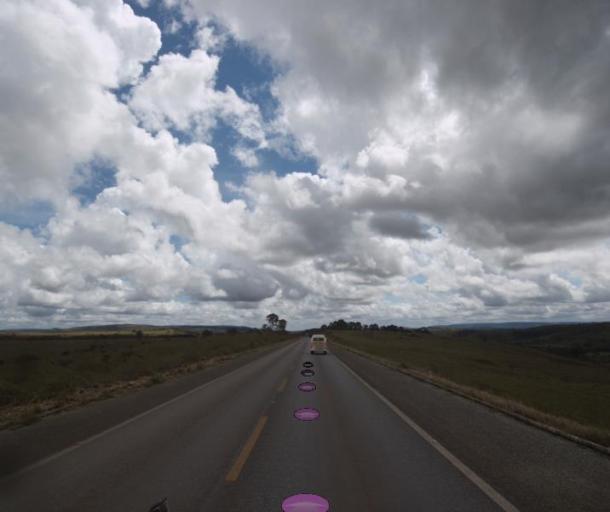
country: BR
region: Goias
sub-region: Pirenopolis
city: Pirenopolis
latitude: -15.7574
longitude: -48.7405
